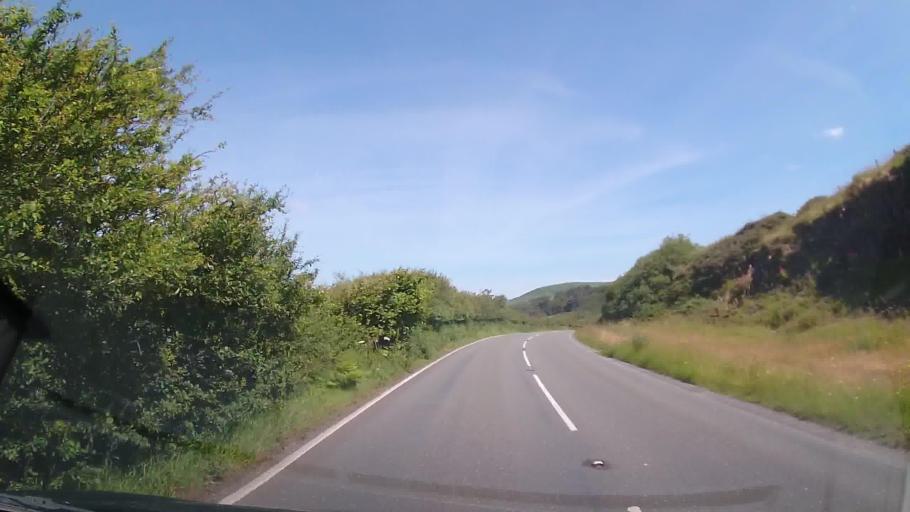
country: GB
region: Wales
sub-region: Gwynedd
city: Tywyn
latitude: 52.5567
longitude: -4.0722
